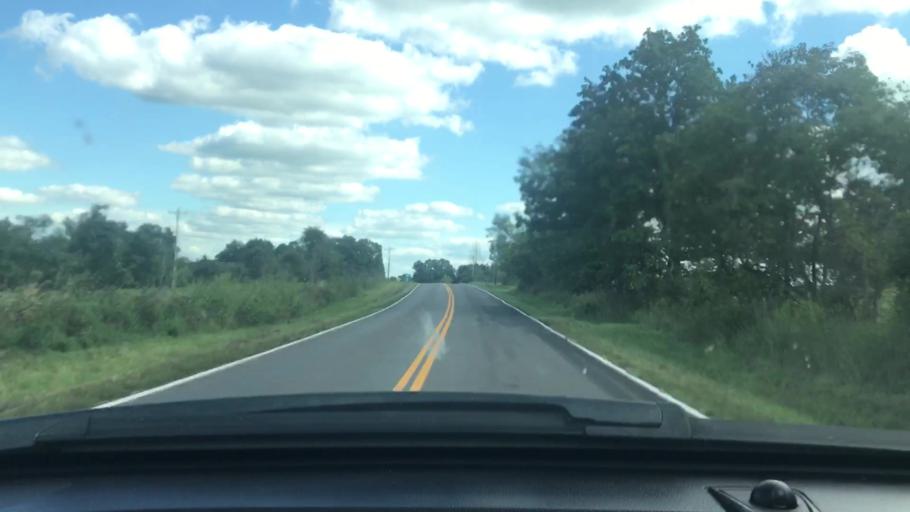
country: US
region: Missouri
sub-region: Wright County
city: Mountain Grove
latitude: 37.3134
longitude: -92.3188
